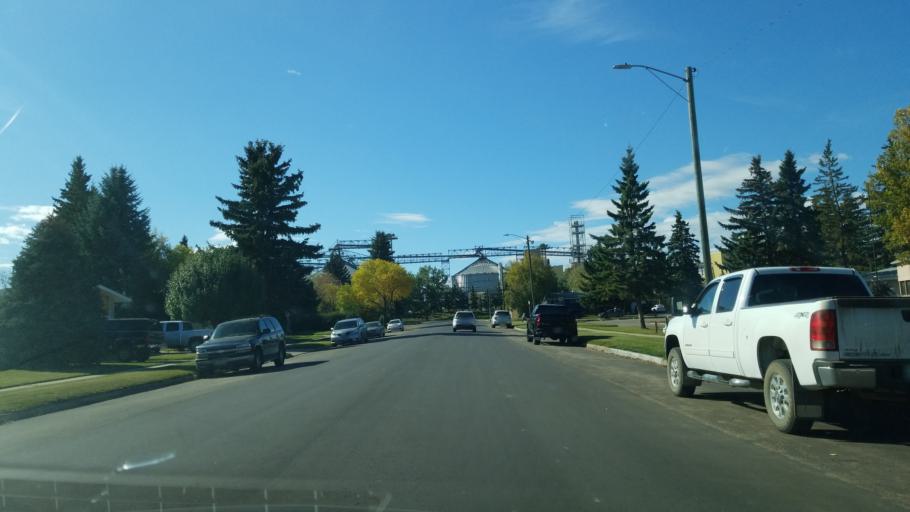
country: CA
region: Saskatchewan
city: Lloydminster
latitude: 53.2834
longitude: -110.0271
